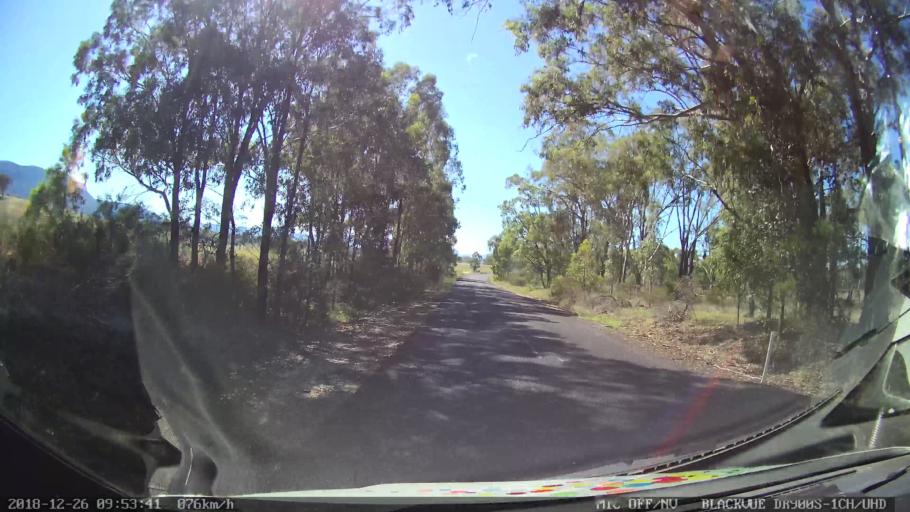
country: AU
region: New South Wales
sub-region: Mid-Western Regional
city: Kandos
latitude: -33.0234
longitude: 150.1548
